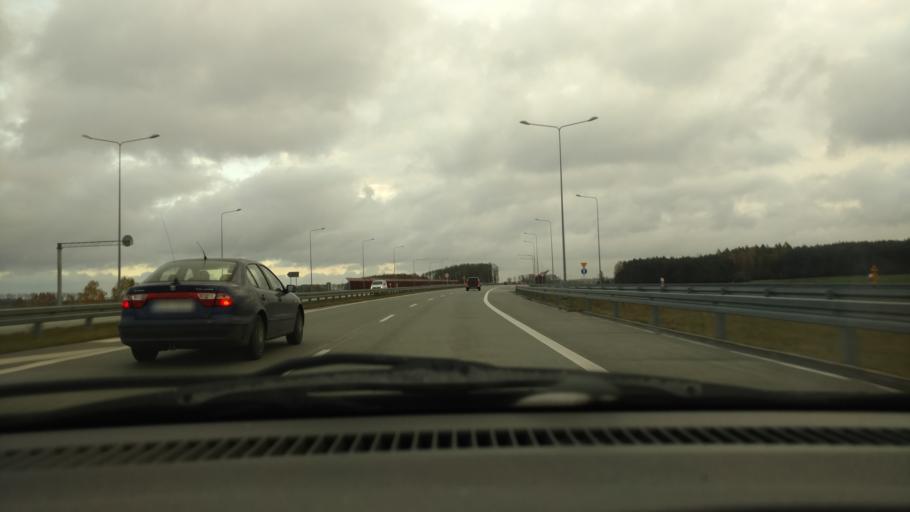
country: PL
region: Lodz Voivodeship
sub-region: Powiat lodzki wschodni
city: Rzgow
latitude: 51.6409
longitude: 19.5075
